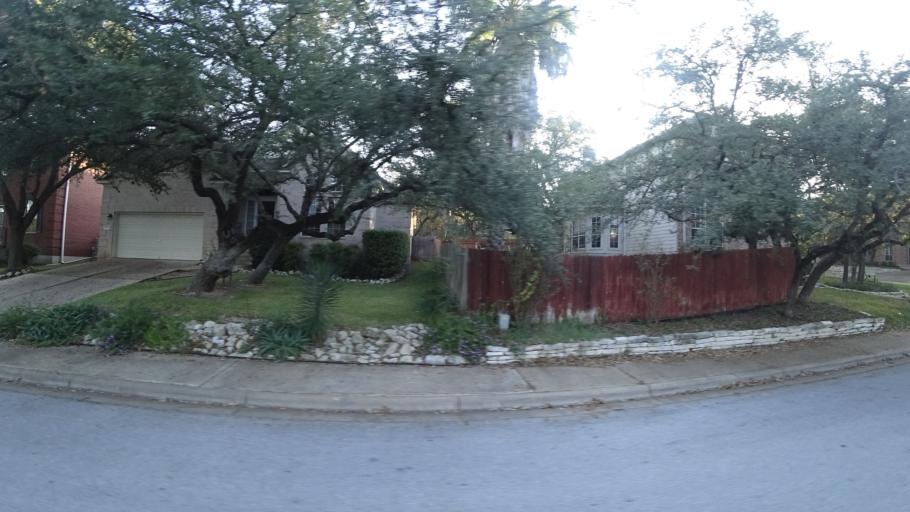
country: US
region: Texas
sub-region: Travis County
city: Hudson Bend
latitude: 30.3794
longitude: -97.8931
